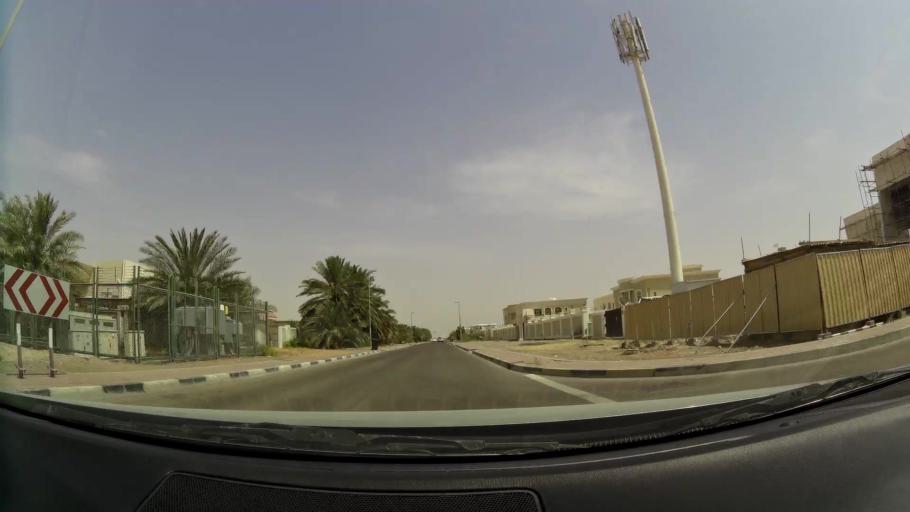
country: AE
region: Abu Dhabi
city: Al Ain
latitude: 24.1808
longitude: 55.7160
